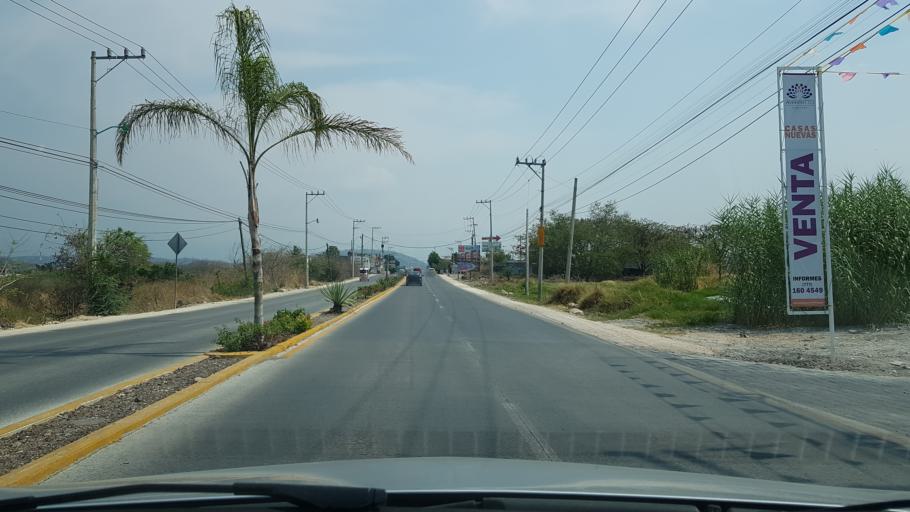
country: MX
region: Morelos
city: Emiliano Zapata
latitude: 18.8142
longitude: -99.1923
